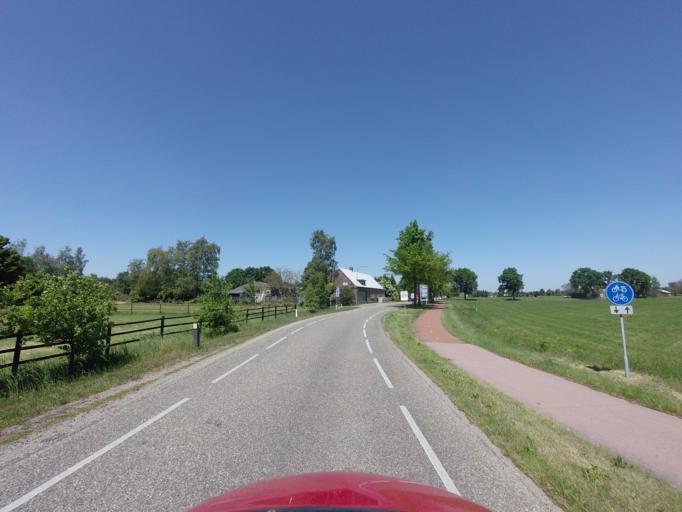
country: BE
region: Flanders
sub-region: Provincie Limburg
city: Lommel
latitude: 51.2638
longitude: 5.3158
